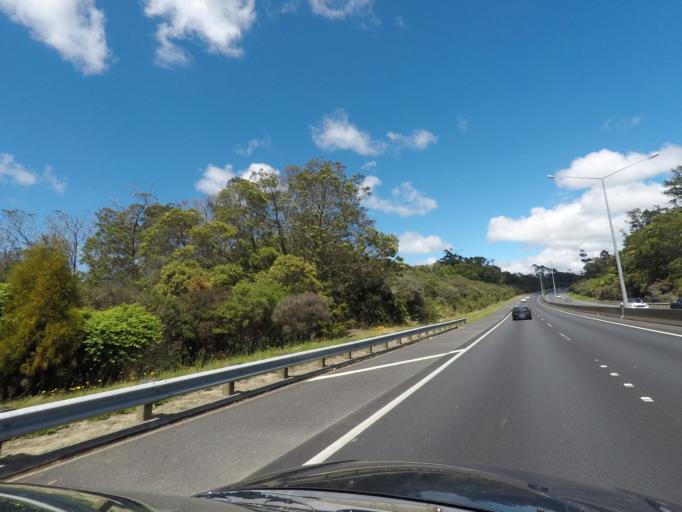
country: NZ
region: Auckland
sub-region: Auckland
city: North Shore
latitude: -36.7725
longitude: 174.6855
